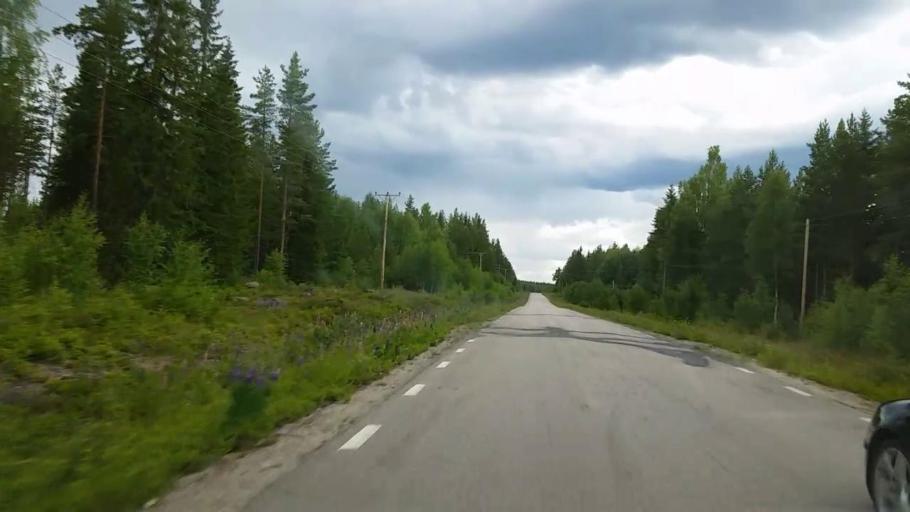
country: SE
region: Gaevleborg
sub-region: Ovanakers Kommun
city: Edsbyn
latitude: 61.4647
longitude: 15.8699
